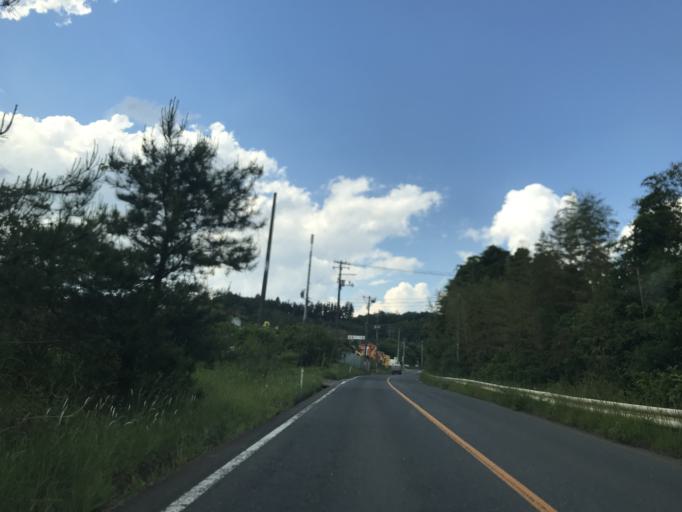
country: JP
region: Miyagi
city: Wakuya
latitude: 38.5603
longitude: 141.1357
